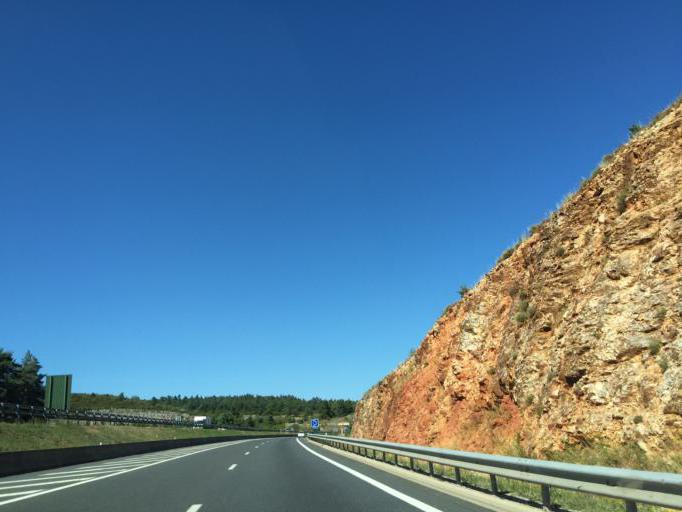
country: FR
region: Midi-Pyrenees
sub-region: Departement de l'Aveyron
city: Severac-le-Chateau
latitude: 44.3524
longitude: 3.1076
